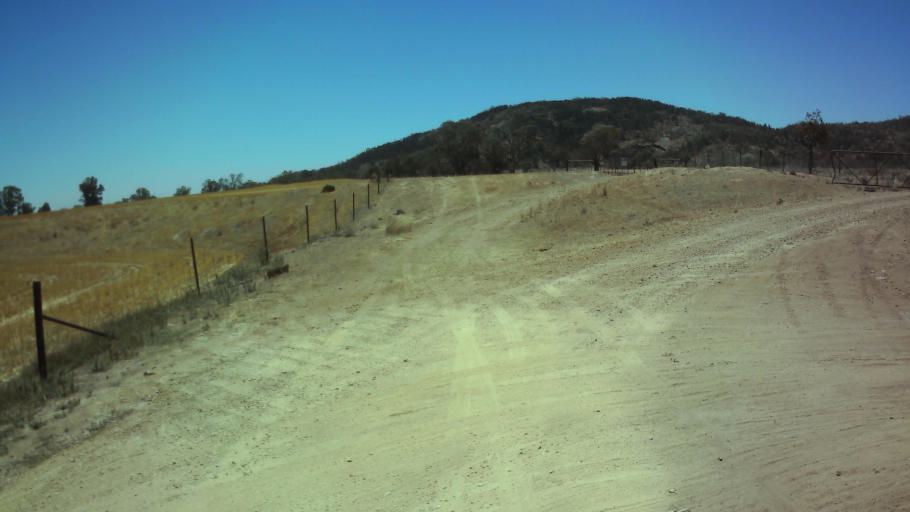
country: AU
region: New South Wales
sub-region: Weddin
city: Grenfell
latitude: -33.8534
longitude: 148.1081
